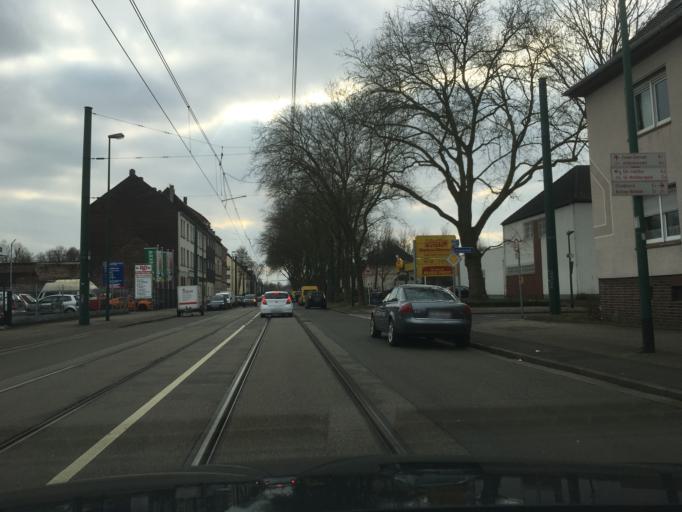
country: DE
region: North Rhine-Westphalia
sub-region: Regierungsbezirk Munster
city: Gladbeck
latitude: 51.5319
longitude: 7.0129
